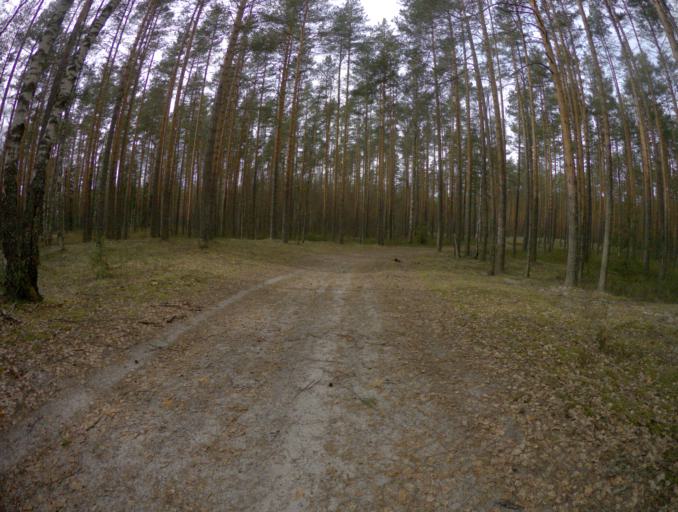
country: RU
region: Vladimir
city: Raduzhnyy
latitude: 55.9464
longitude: 40.2760
